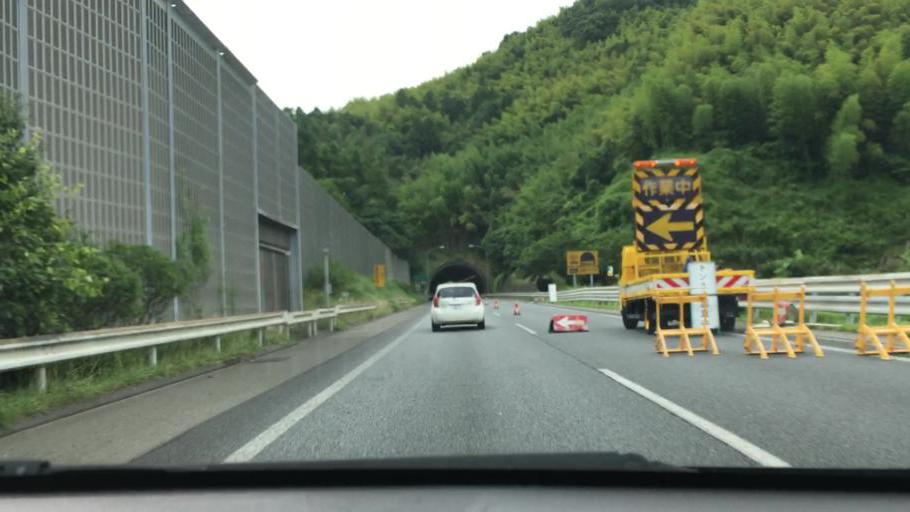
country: JP
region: Yamaguchi
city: Tokuyama
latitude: 34.0883
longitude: 131.7773
